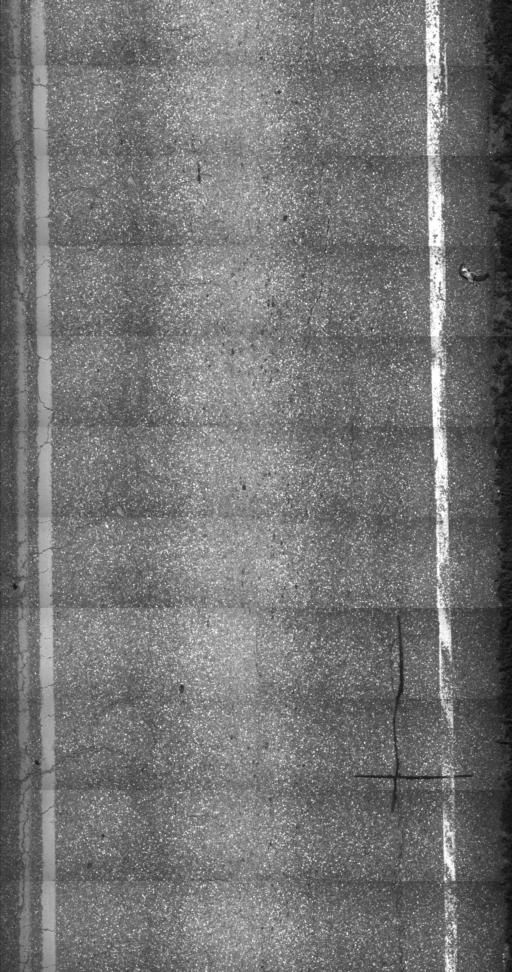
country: US
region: Vermont
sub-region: Franklin County
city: Enosburg Falls
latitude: 44.7858
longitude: -72.8604
